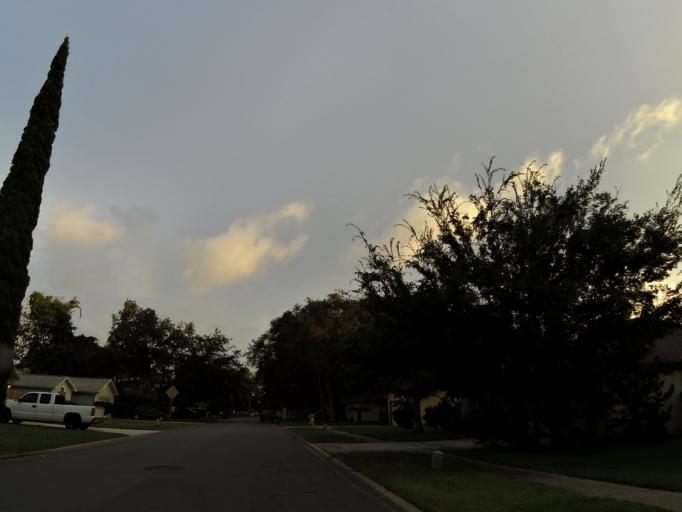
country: US
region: Florida
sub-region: Duval County
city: Atlantic Beach
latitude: 30.3632
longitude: -81.4905
